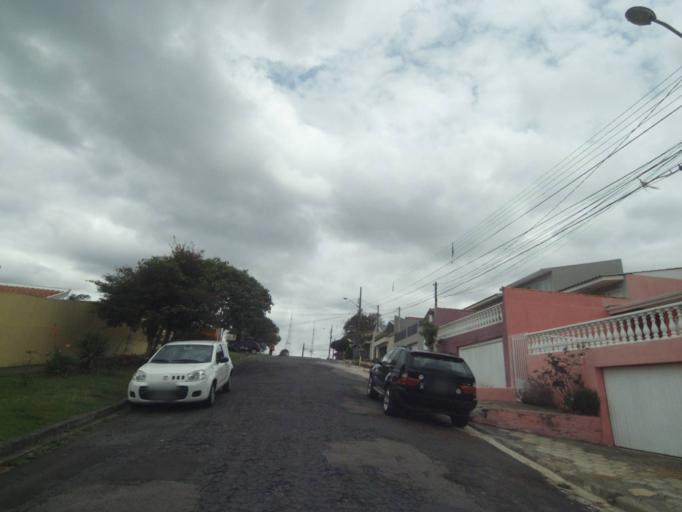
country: BR
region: Parana
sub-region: Curitiba
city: Curitiba
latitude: -25.3899
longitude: -49.2879
